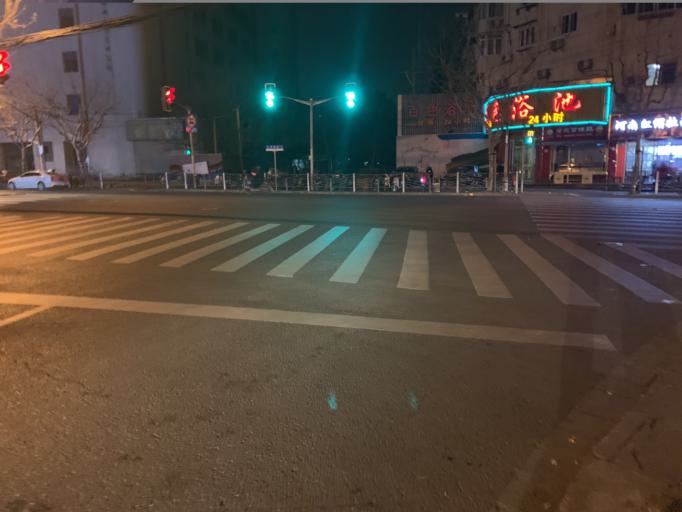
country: CN
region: Shanghai Shi
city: Changqiao
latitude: 31.1449
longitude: 121.4290
